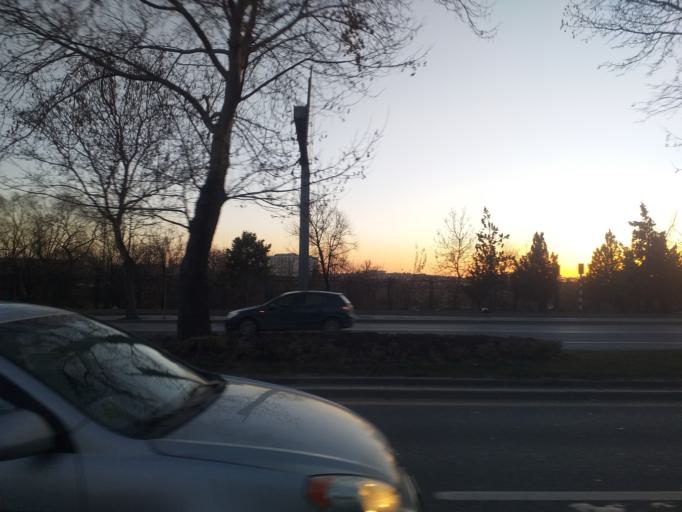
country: TR
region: Ankara
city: Ankara
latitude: 39.9496
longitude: 32.8259
